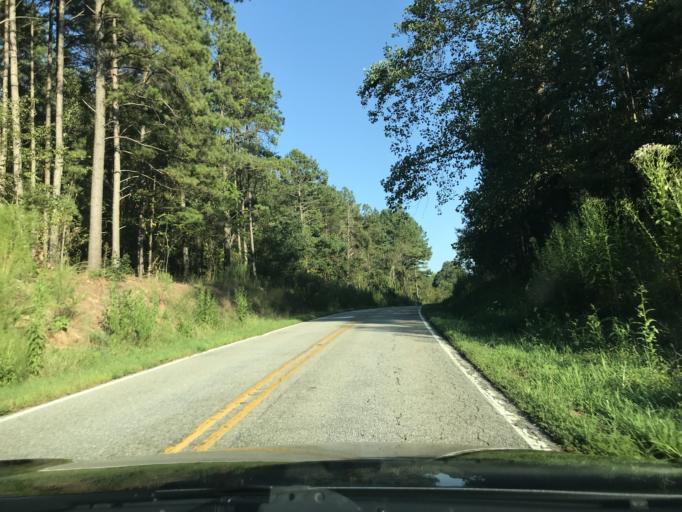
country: US
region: South Carolina
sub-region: Spartanburg County
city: Mayo
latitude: 35.1071
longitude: -81.7785
